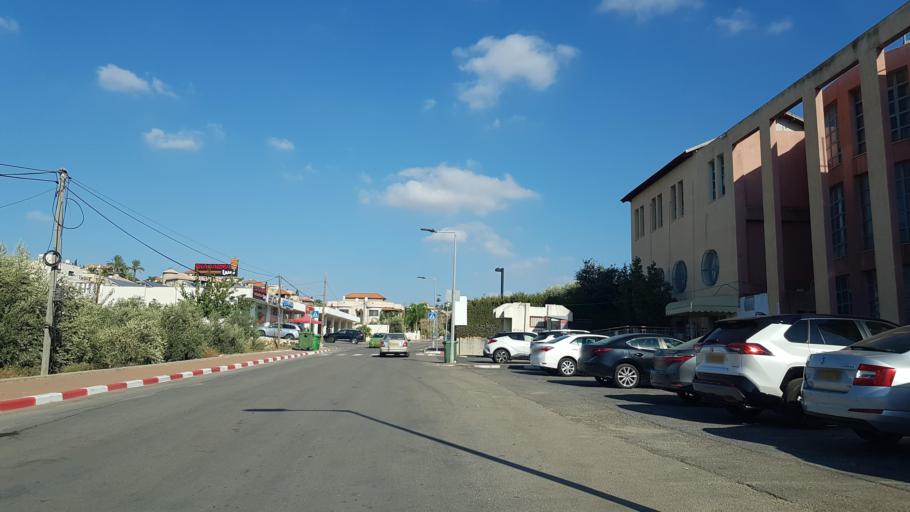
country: PS
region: West Bank
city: Zayta
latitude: 32.3676
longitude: 35.0345
